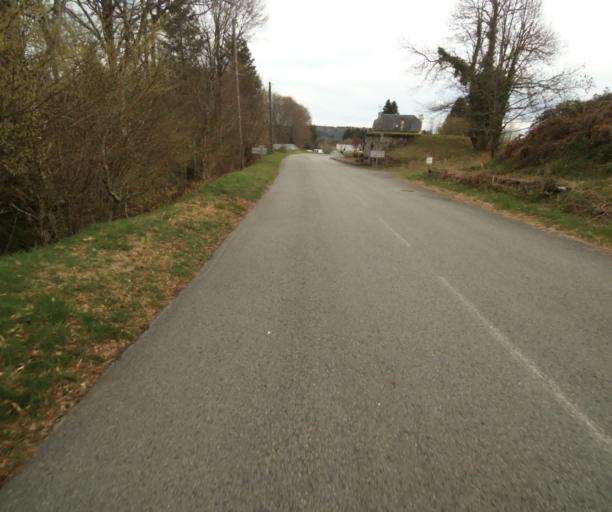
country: FR
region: Limousin
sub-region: Departement de la Correze
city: Argentat
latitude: 45.1999
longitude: 1.9624
